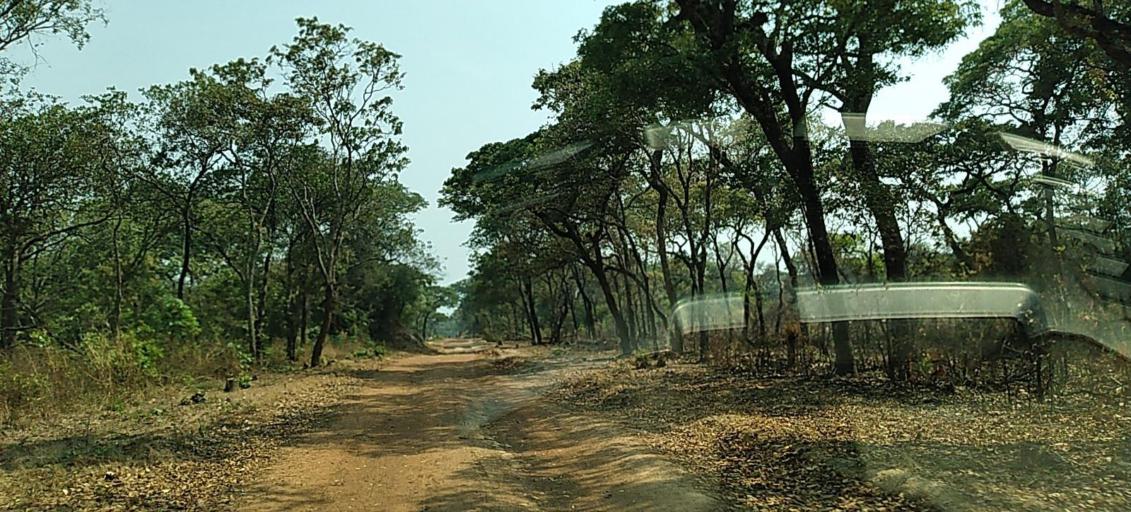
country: ZM
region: North-Western
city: Kansanshi
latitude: -12.0727
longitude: 26.8879
